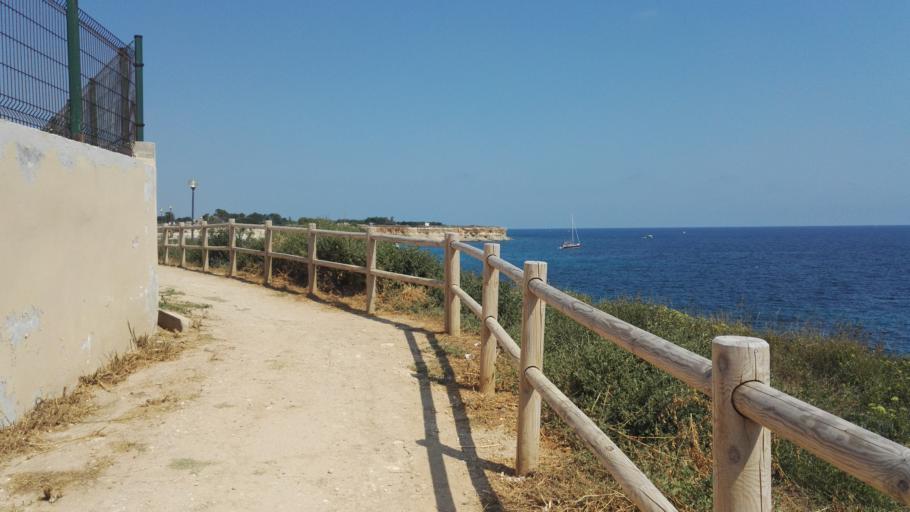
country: IT
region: Apulia
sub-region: Provincia di Lecce
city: Borgagne
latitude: 40.2553
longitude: 18.4456
